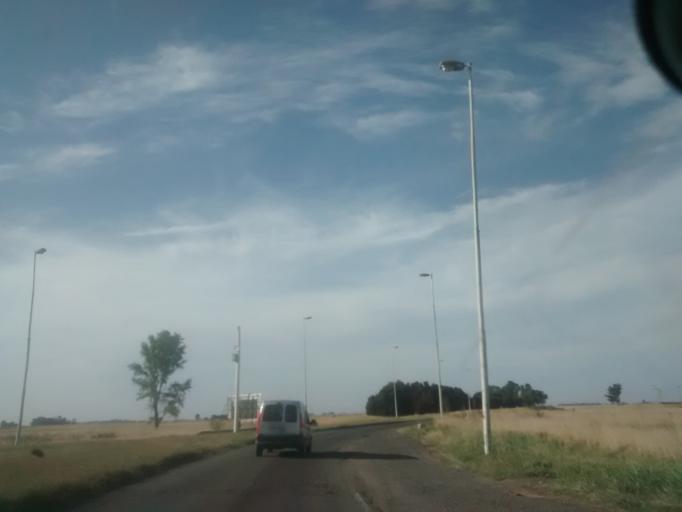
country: AR
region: Buenos Aires
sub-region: Partido de Ayacucho
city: Ayacucho
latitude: -37.1263
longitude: -58.5511
